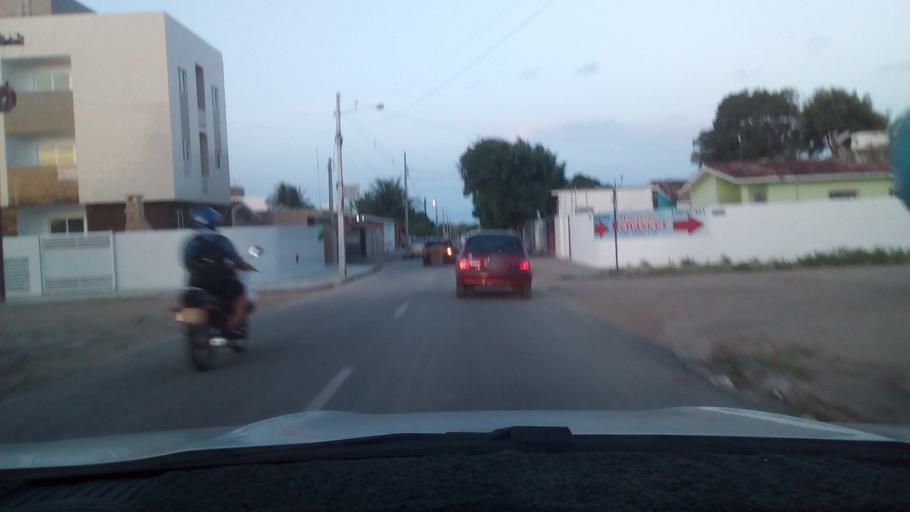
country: BR
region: Paraiba
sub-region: Bayeux
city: Bayeux
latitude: -7.1769
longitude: -34.9184
